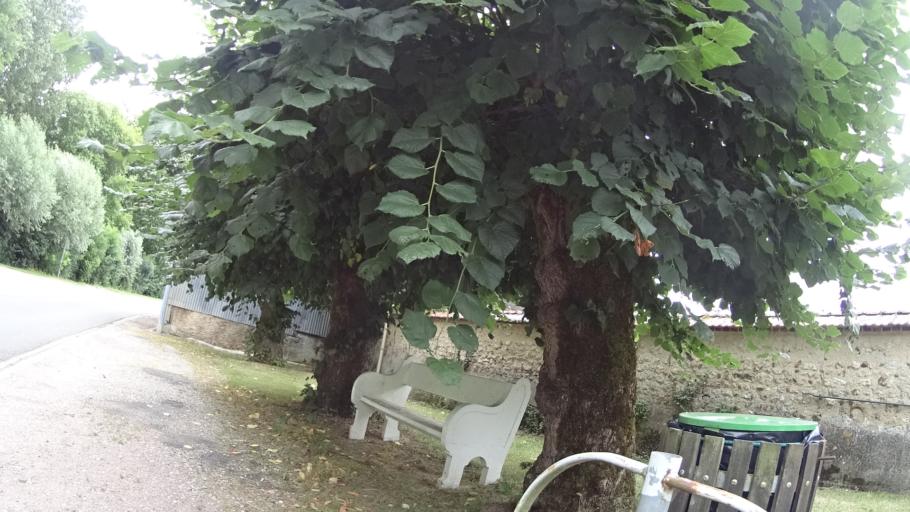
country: FR
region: Centre
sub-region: Departement du Loiret
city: Saint-Germain-des-Pres
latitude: 47.9466
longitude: 2.8535
